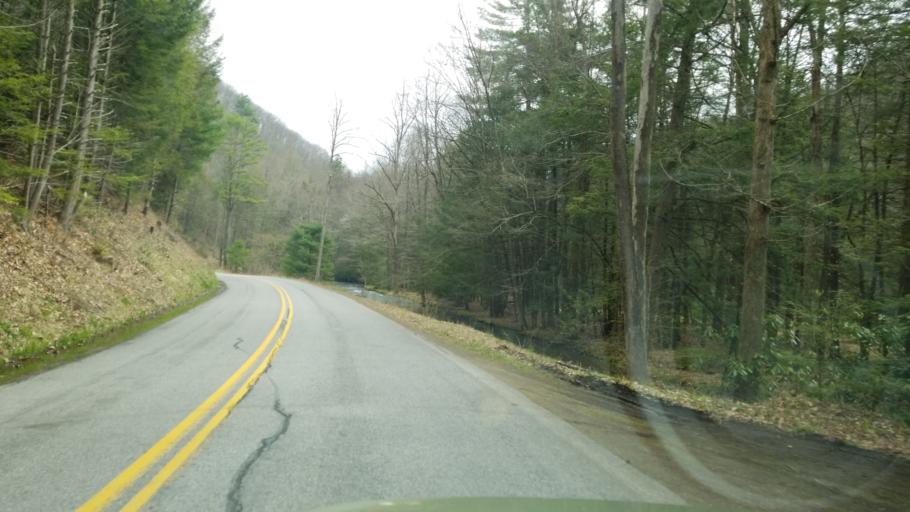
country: US
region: Pennsylvania
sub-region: Cameron County
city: Emporium
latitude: 41.2868
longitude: -78.1239
